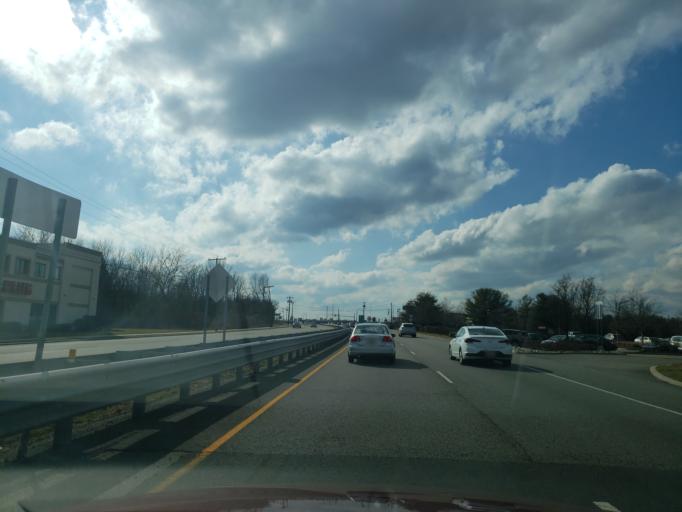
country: US
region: New Jersey
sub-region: Hunterdon County
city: Flemington
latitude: 40.5046
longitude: -74.8490
